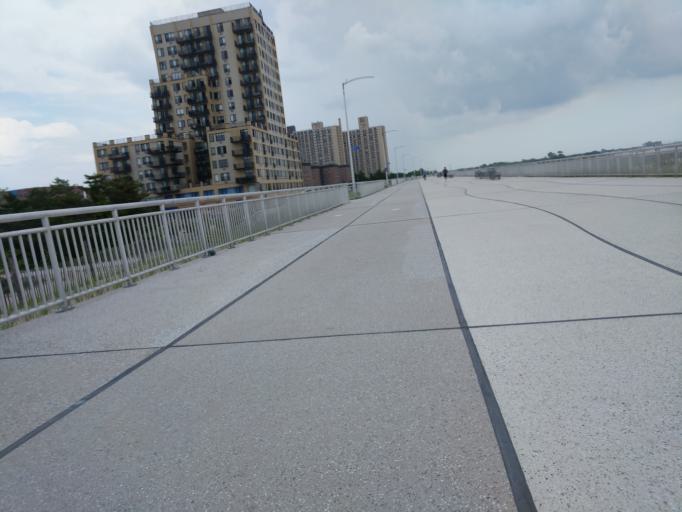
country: US
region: New York
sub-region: Nassau County
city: Atlantic Beach
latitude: 40.5922
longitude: -73.7600
